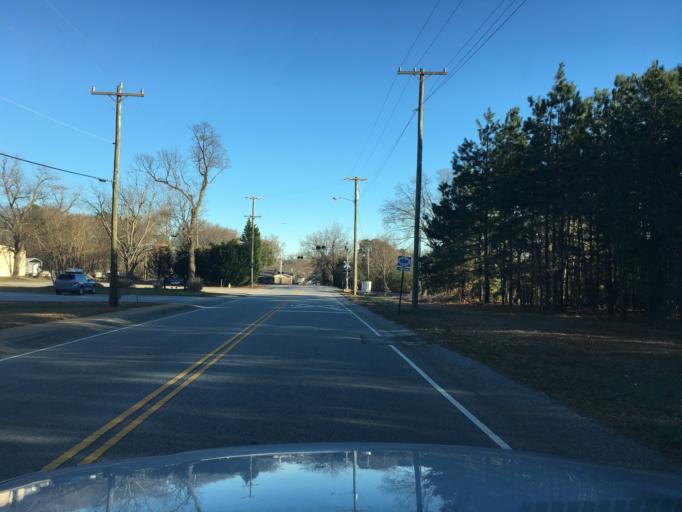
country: US
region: South Carolina
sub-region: Greenville County
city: Greer
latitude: 34.9384
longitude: -82.2443
